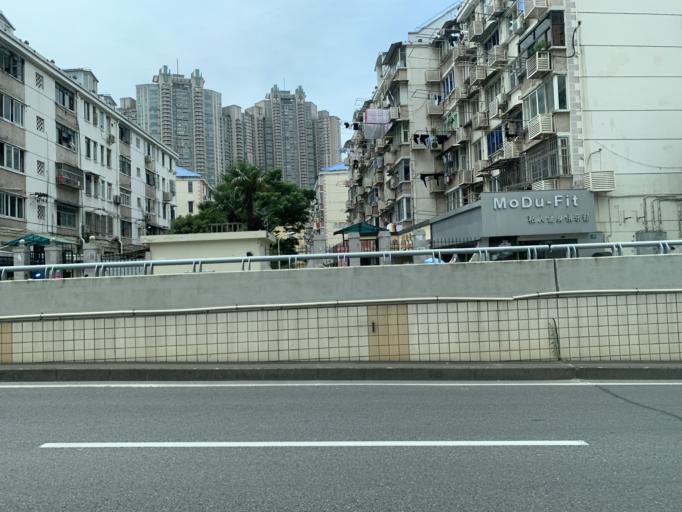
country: CN
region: Shanghai Shi
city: Pudong
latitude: 31.2272
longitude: 121.5127
